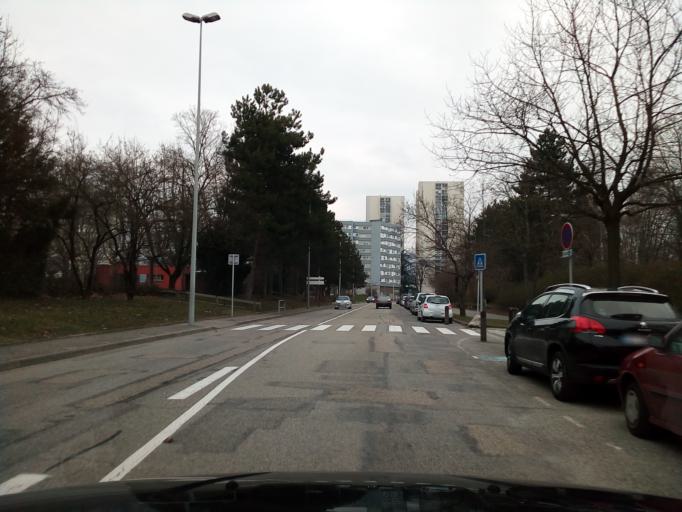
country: FR
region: Rhone-Alpes
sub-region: Departement de l'Isere
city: Echirolles
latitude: 45.1541
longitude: 5.7234
